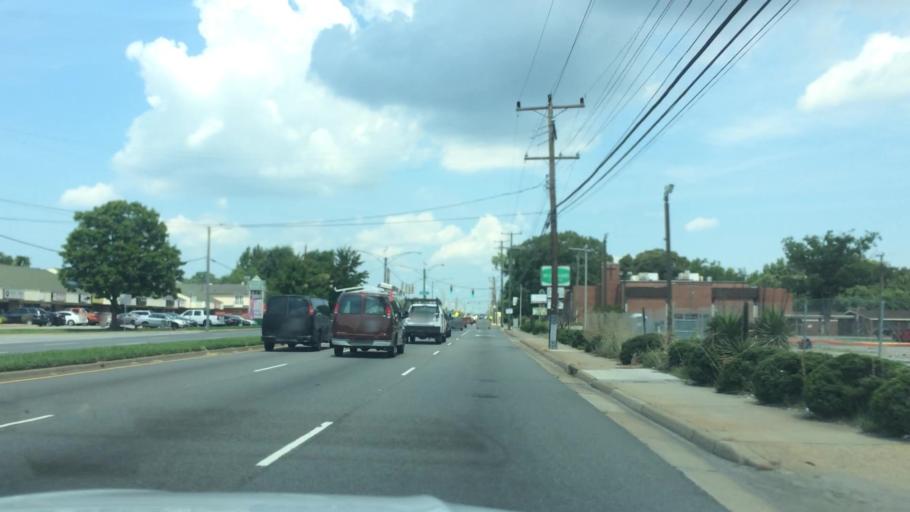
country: US
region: Virginia
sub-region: City of Newport News
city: Newport News
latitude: 37.0228
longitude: -76.4465
